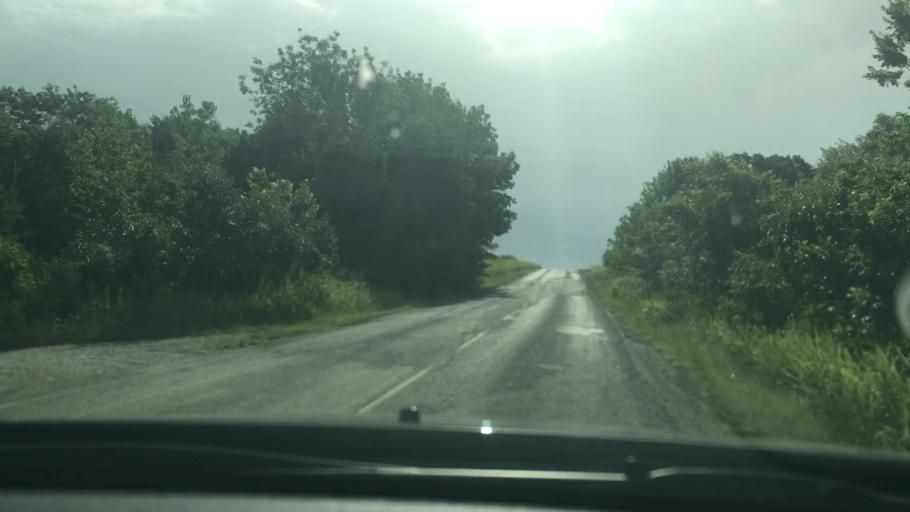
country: US
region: Oklahoma
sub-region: Pontotoc County
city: Byng
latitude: 34.8737
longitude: -96.5829
